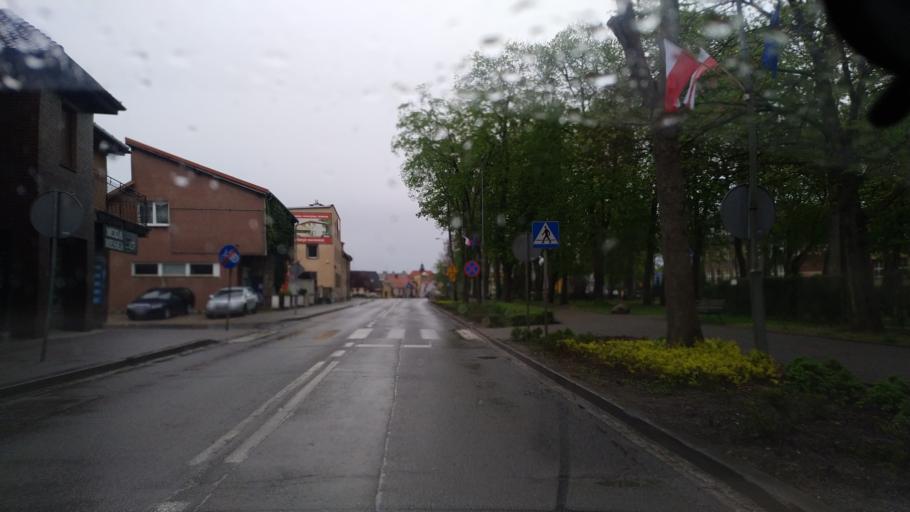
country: PL
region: Greater Poland Voivodeship
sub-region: Powiat zlotowski
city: Zlotow
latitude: 53.3607
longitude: 17.0374
